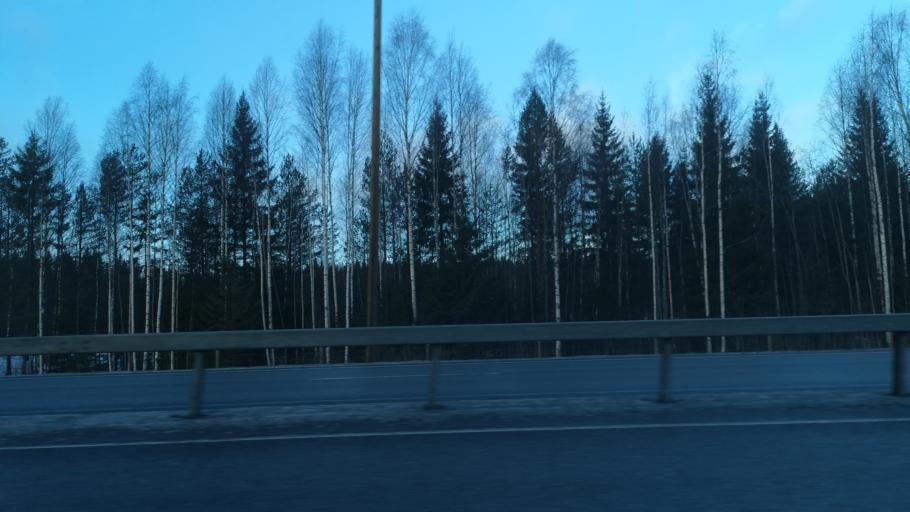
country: FI
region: Southern Savonia
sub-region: Mikkeli
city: Maentyharju
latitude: 61.5321
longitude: 26.8717
